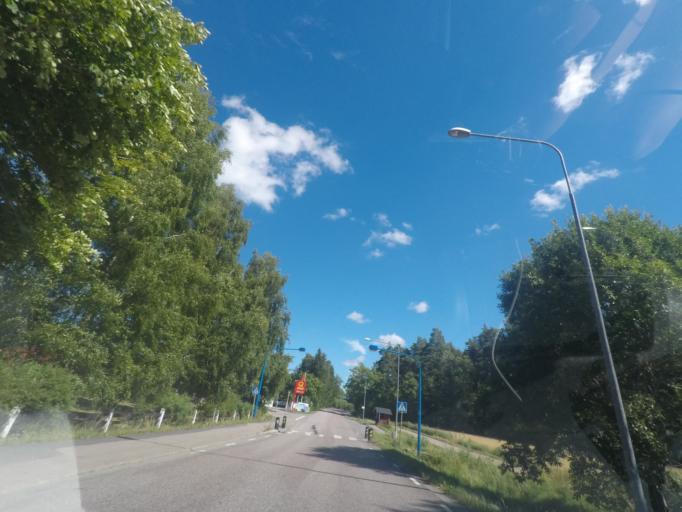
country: SE
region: Uppsala
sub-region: Knivsta Kommun
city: Knivsta
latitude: 59.8766
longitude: 17.9641
